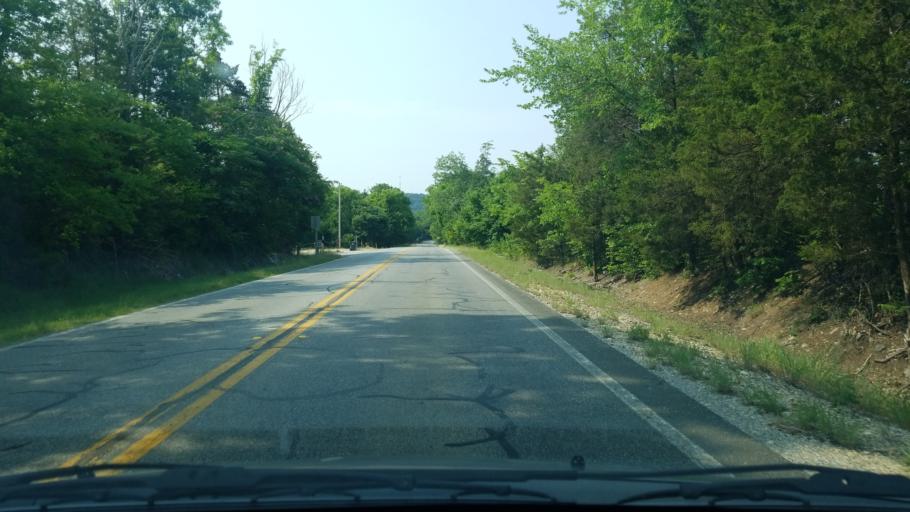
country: US
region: Georgia
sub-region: Catoosa County
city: Ringgold
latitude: 34.9237
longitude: -85.1042
